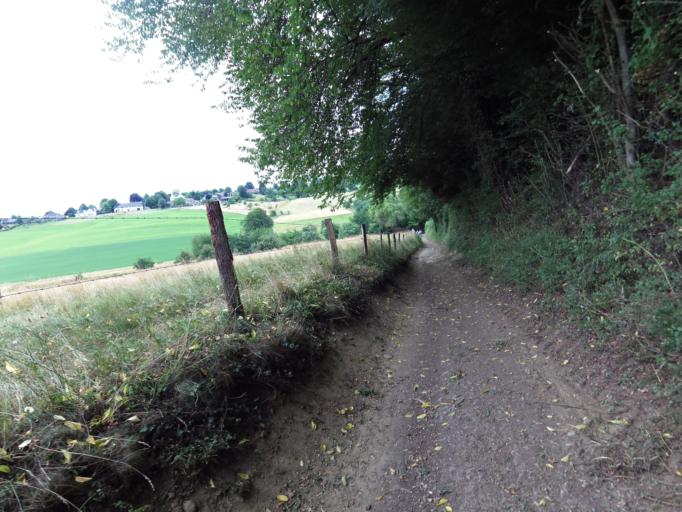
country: NL
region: Limburg
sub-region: Valkenburg aan de Geul
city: Schin op Geul
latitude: 50.7897
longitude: 5.9043
